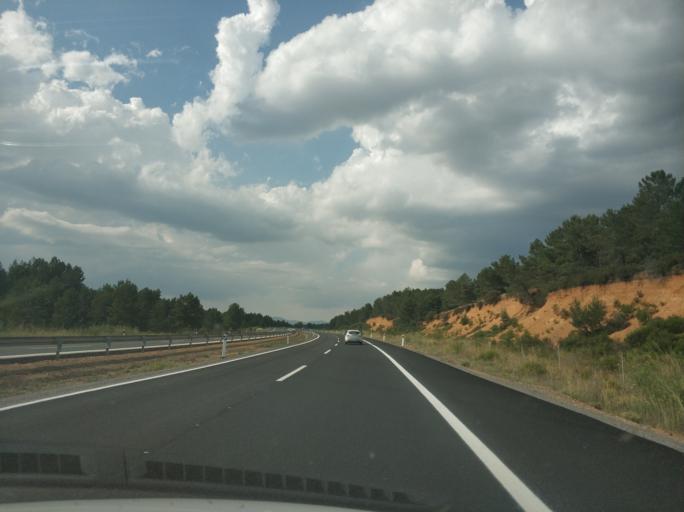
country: ES
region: Castille and Leon
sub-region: Provincia de Leon
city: Cimanes del Tejar
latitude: 42.6571
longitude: -5.7505
